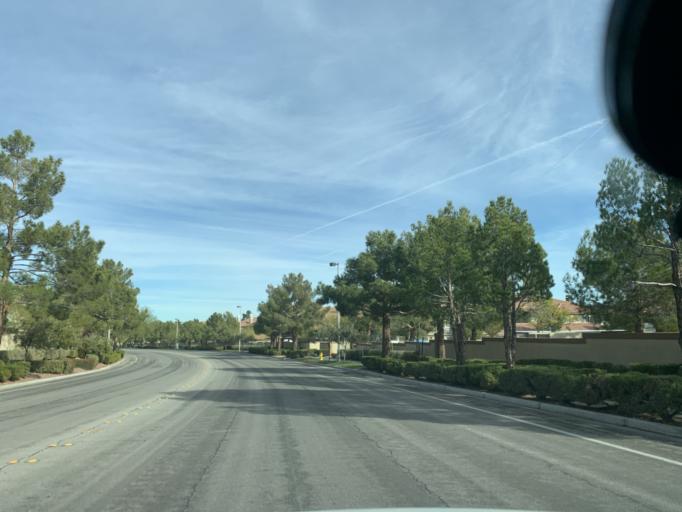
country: US
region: Nevada
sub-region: Clark County
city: Summerlin South
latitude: 36.1475
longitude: -115.3038
